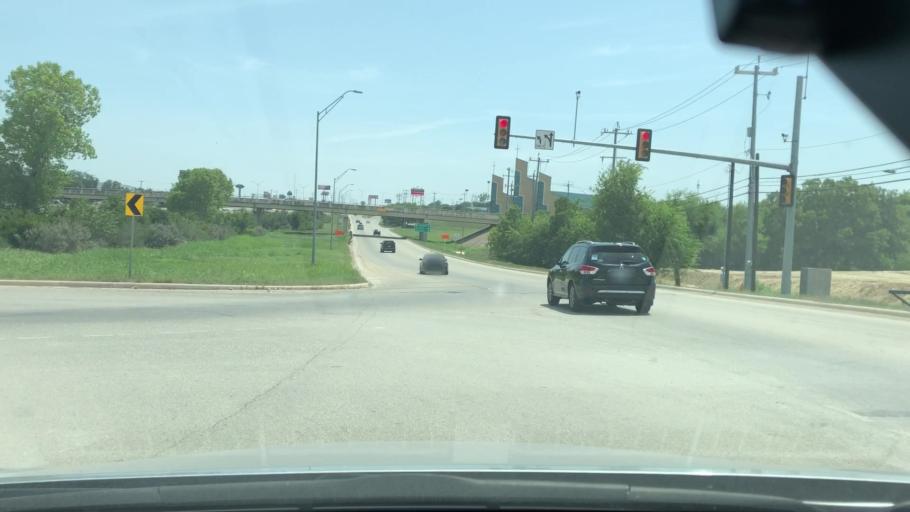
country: US
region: Texas
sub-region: Bexar County
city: Live Oak
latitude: 29.5631
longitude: -98.3410
